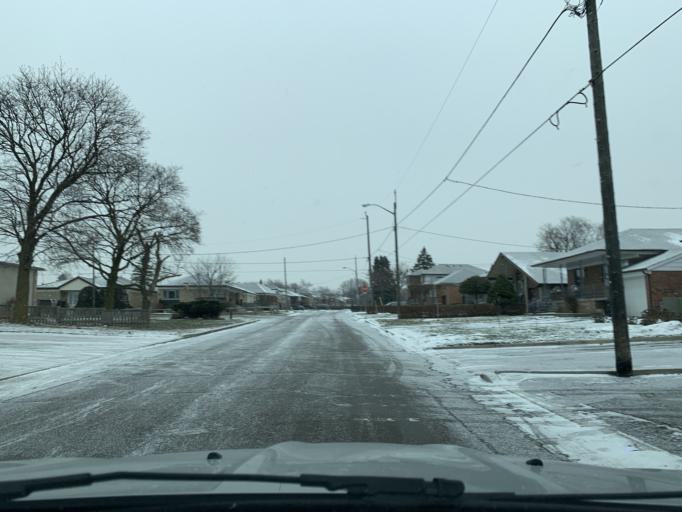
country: CA
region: Ontario
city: Concord
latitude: 43.7346
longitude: -79.4909
